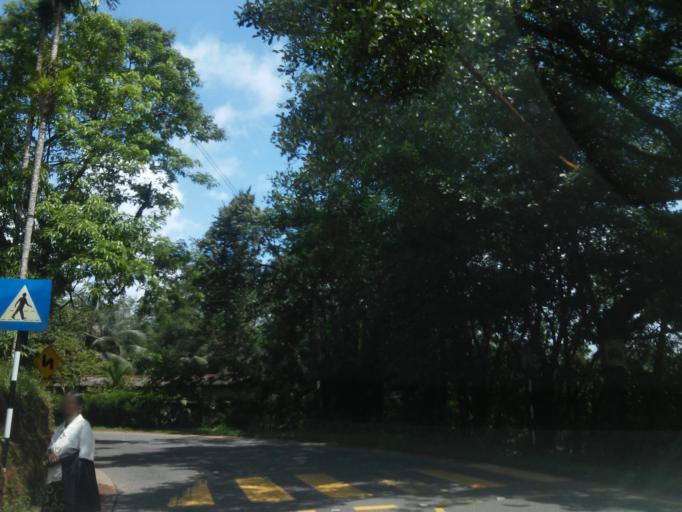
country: LK
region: Sabaragamuwa
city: Ratnapura
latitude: 6.7271
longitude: 80.3274
